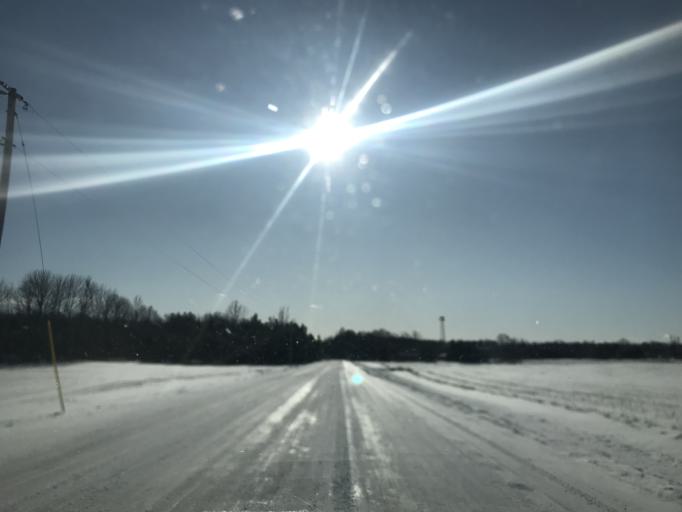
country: US
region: Wisconsin
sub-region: Door County
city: Sturgeon Bay
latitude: 44.8271
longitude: -87.5041
